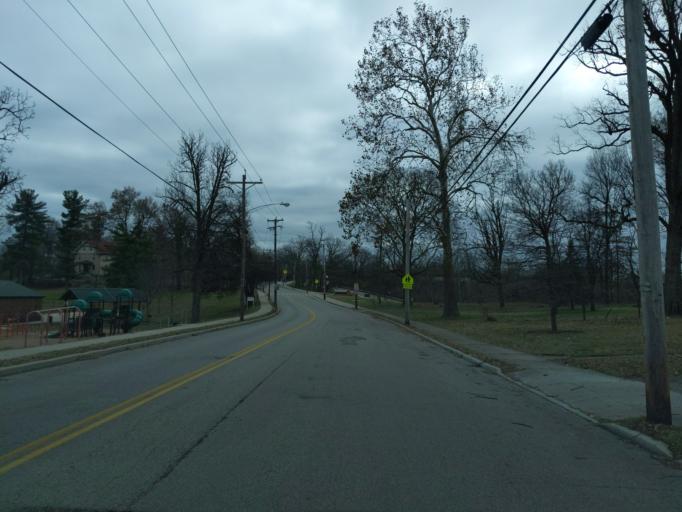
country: US
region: Ohio
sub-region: Hamilton County
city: North College Hill
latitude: 39.1938
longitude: -84.5505
